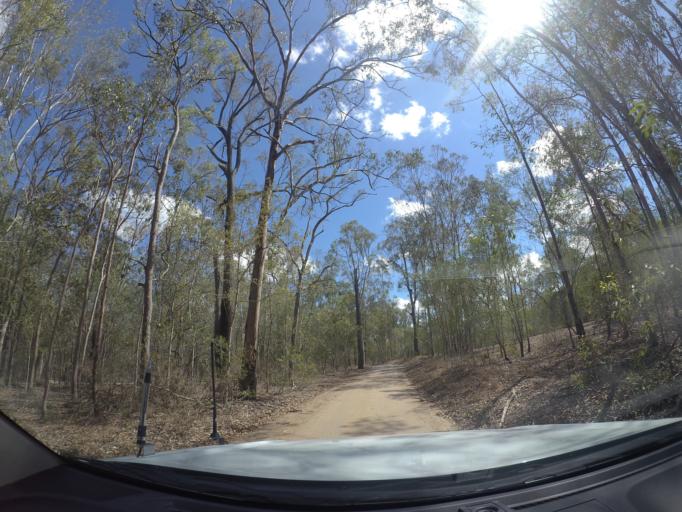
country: AU
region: Queensland
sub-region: Logan
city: North Maclean
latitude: -27.8207
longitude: 152.9694
